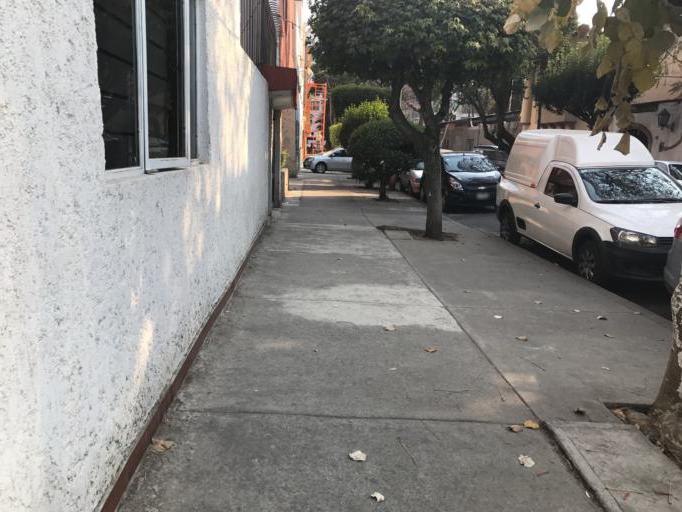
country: MX
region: Mexico City
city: Benito Juarez
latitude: 19.3938
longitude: -99.1519
